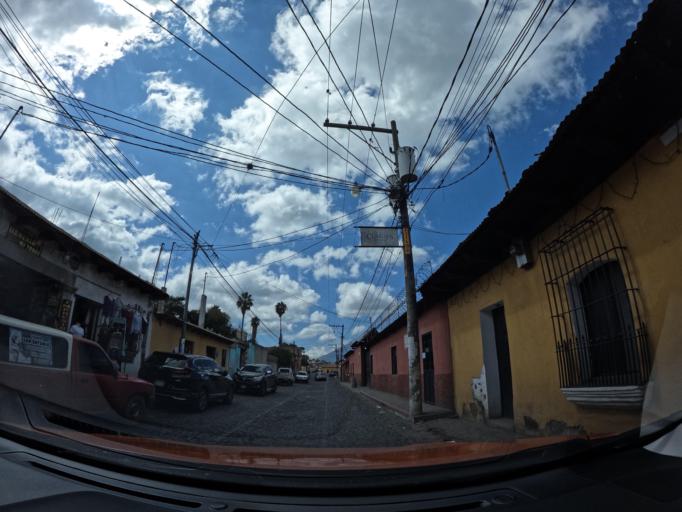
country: GT
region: Sacatepequez
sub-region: Municipio de Santa Maria de Jesus
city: Santa Maria de Jesus
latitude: 14.5314
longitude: -90.7389
